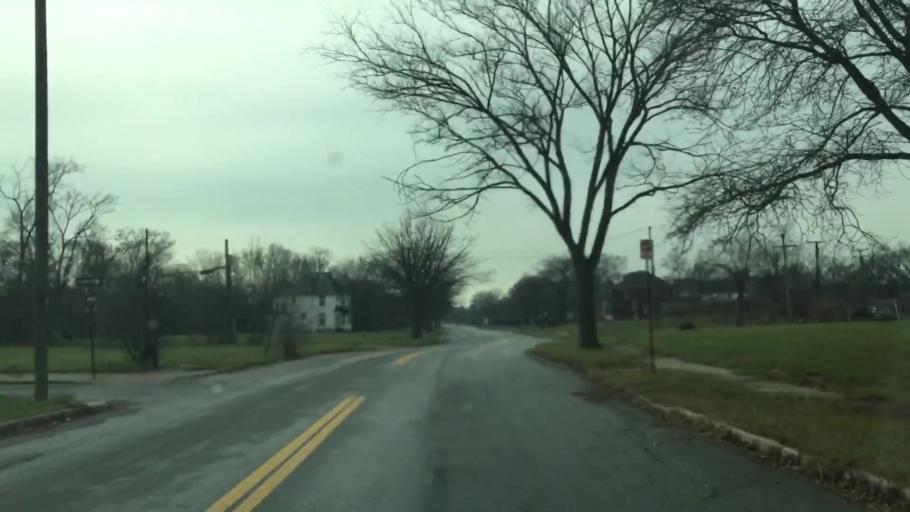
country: US
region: Michigan
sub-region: Wayne County
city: Highland Park
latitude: 42.3509
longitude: -83.1053
